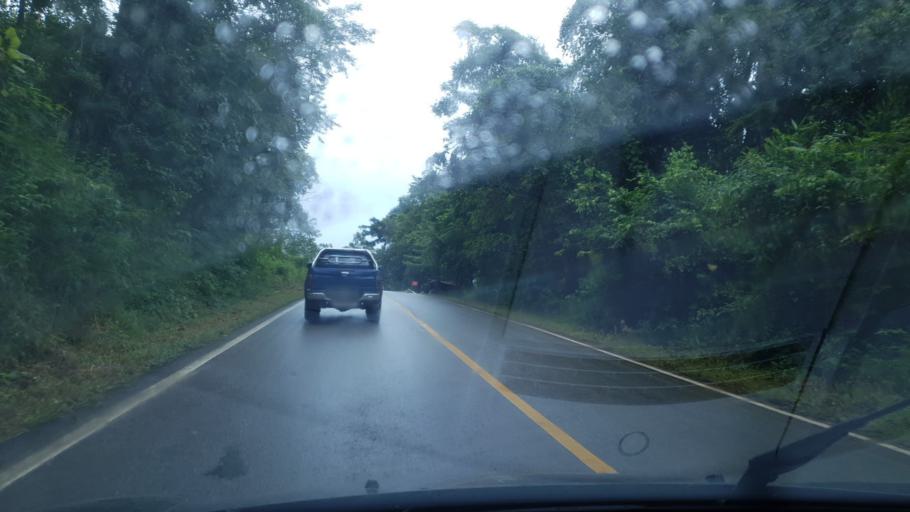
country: TH
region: Mae Hong Son
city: Mae La Noi
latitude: 18.2936
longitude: 97.9183
